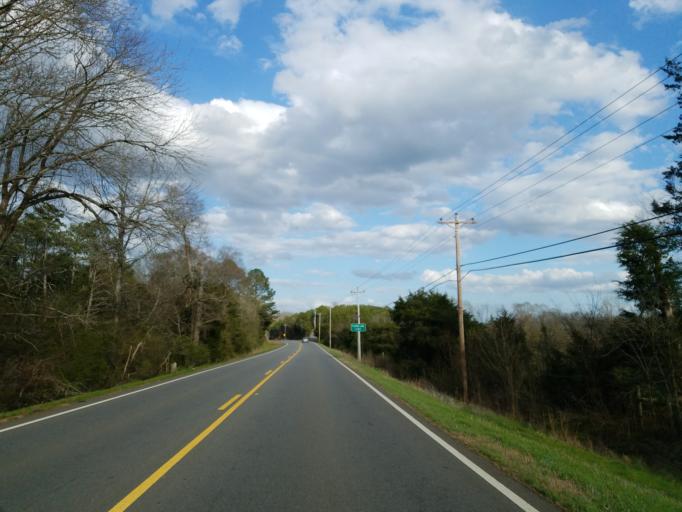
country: US
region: Georgia
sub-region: Bartow County
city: Rydal
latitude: 34.4477
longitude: -84.7995
